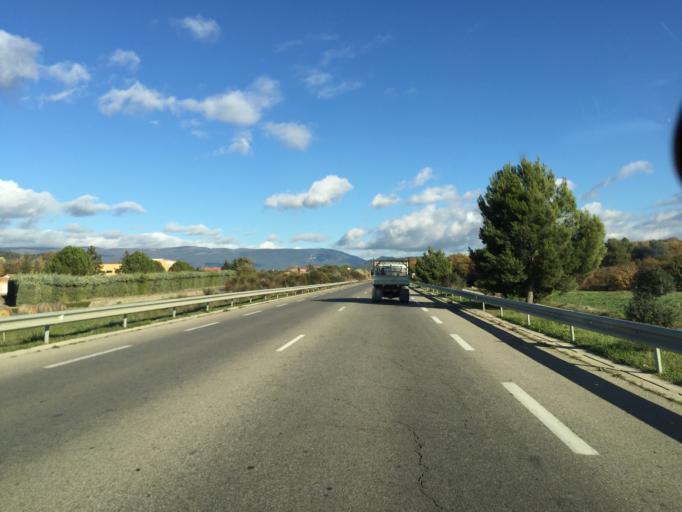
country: FR
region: Provence-Alpes-Cote d'Azur
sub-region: Departement du Vaucluse
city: Gargas
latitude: 43.8812
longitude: 5.3481
